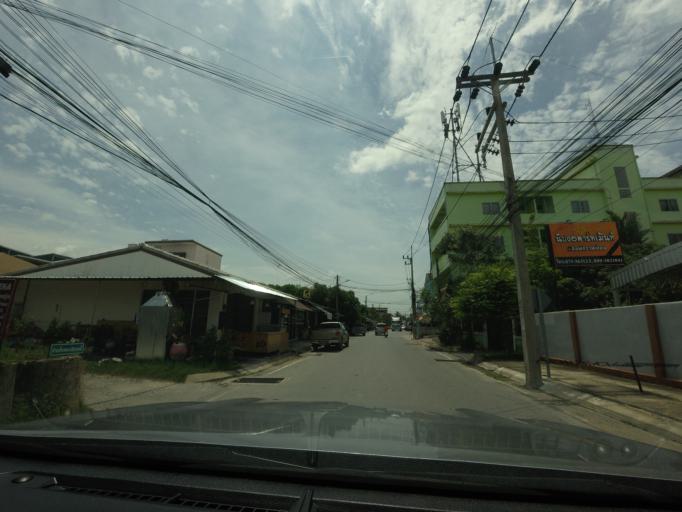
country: TH
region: Yala
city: Yala
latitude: 6.5435
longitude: 101.2934
